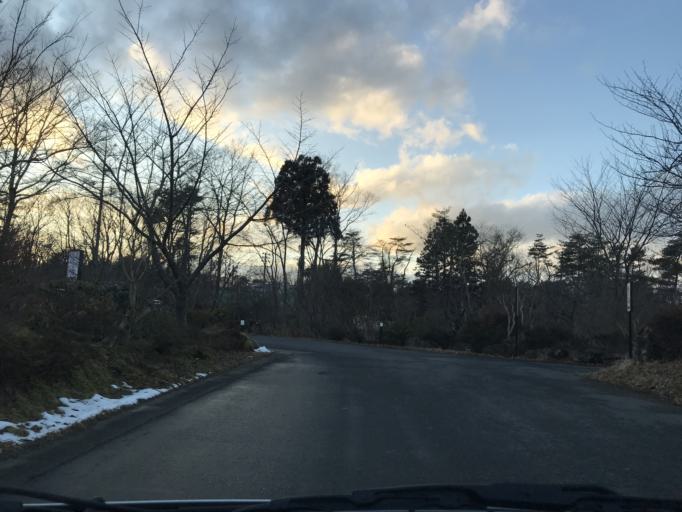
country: JP
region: Iwate
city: Ichinoseki
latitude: 38.9511
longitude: 141.1060
